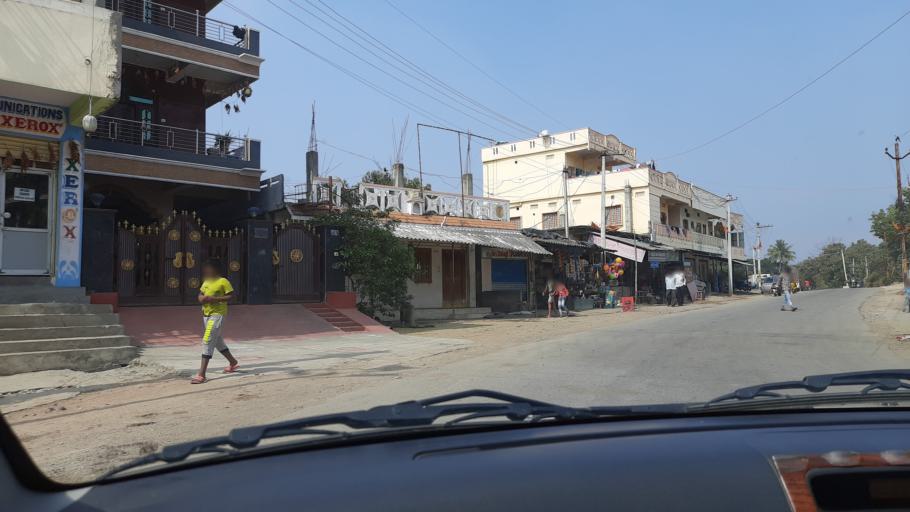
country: IN
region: Telangana
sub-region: Rangareddi
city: Lal Bahadur Nagar
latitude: 17.2716
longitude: 78.6694
